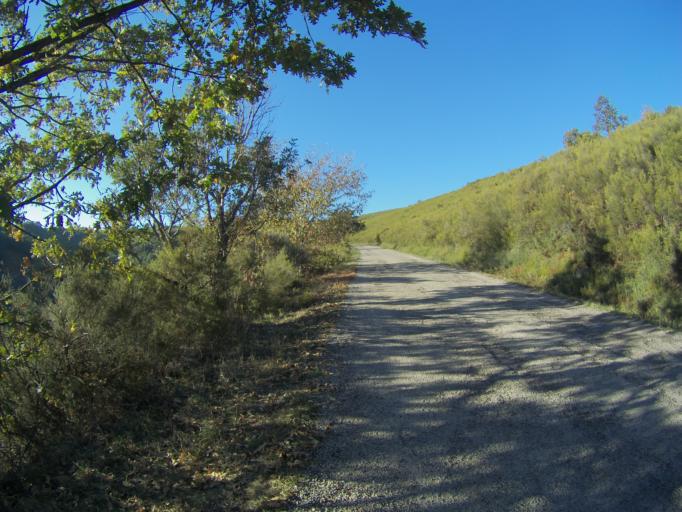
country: ES
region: Castille and Leon
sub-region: Provincia de Leon
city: Vega de Valcarce
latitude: 42.6949
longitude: -7.0111
